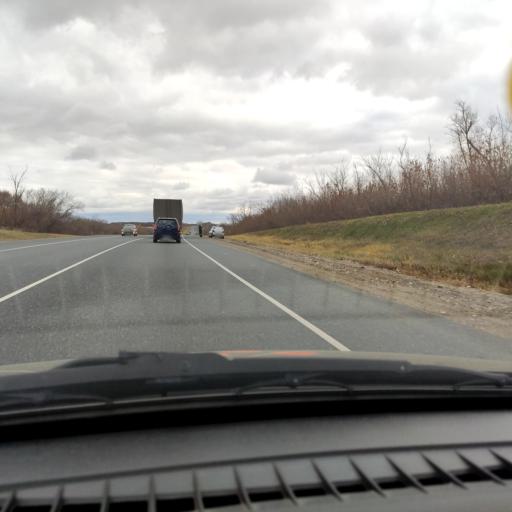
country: RU
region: Samara
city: Mezhdurechensk
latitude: 53.2540
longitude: 49.0405
